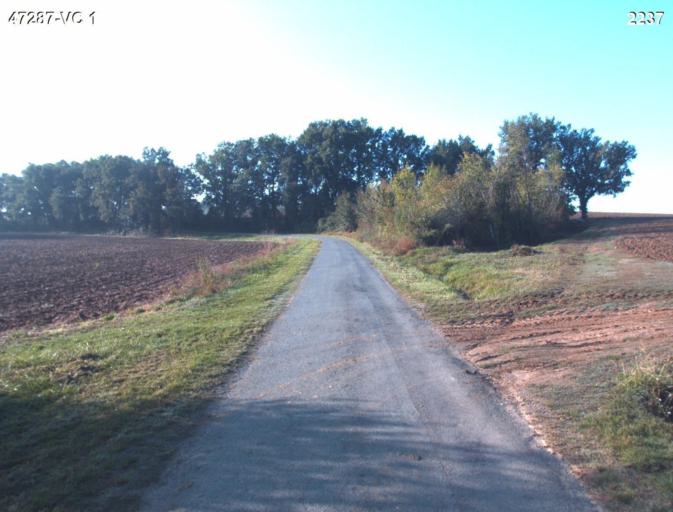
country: FR
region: Aquitaine
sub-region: Departement du Lot-et-Garonne
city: Sainte-Colombe-en-Bruilhois
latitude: 44.1407
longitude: 0.4462
